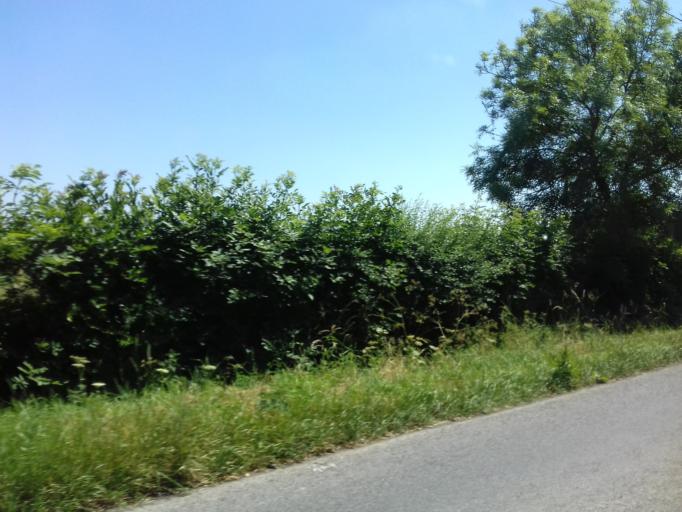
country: IE
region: Leinster
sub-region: An Mhi
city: Ashbourne
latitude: 53.5521
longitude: -6.3254
